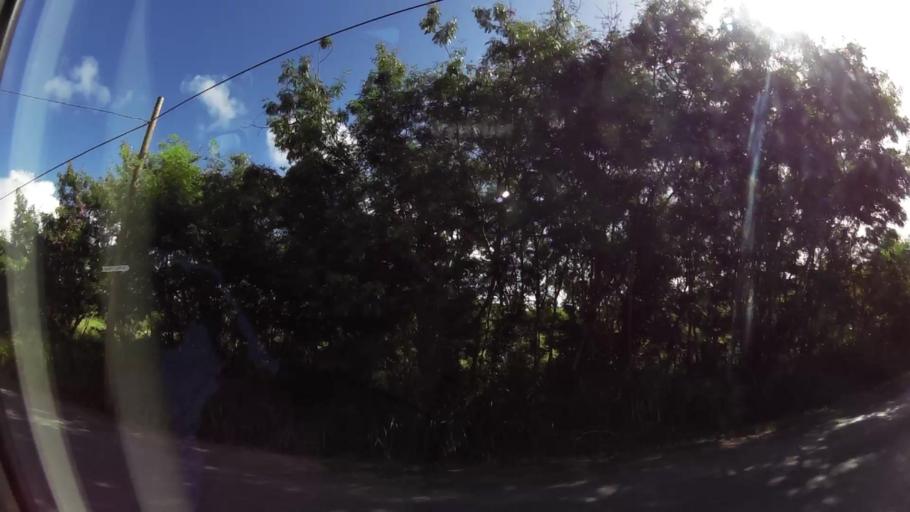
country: BB
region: Saint James
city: Holetown
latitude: 13.2028
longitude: -59.6174
